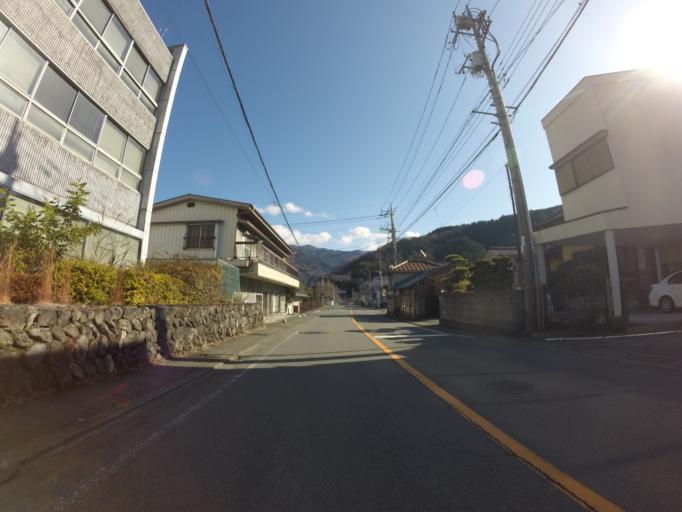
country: JP
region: Shizuoka
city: Fujinomiya
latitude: 35.3711
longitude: 138.4359
